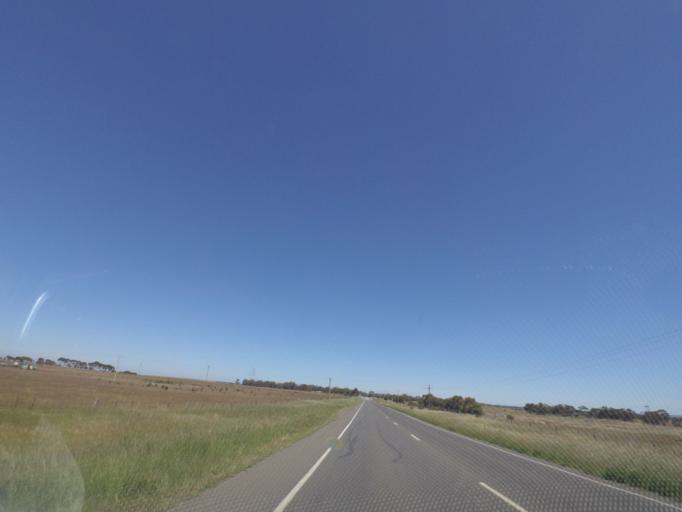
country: AU
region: Victoria
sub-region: Melton
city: Brookfield
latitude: -37.6826
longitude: 144.5036
